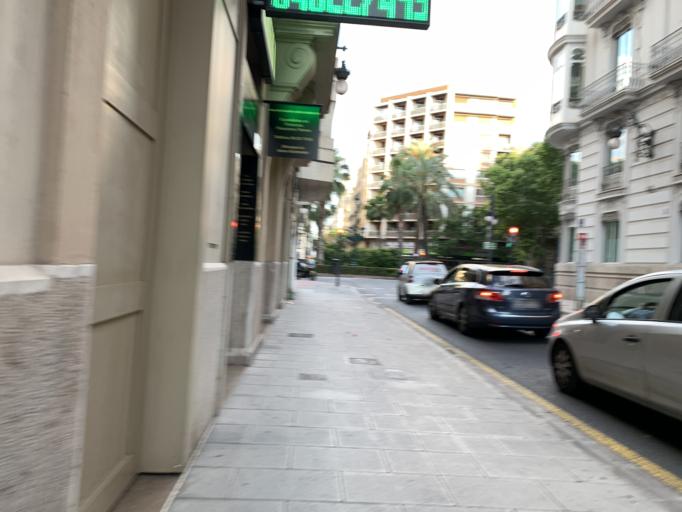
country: ES
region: Valencia
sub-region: Provincia de Valencia
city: Valencia
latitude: 39.4661
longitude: -0.3725
